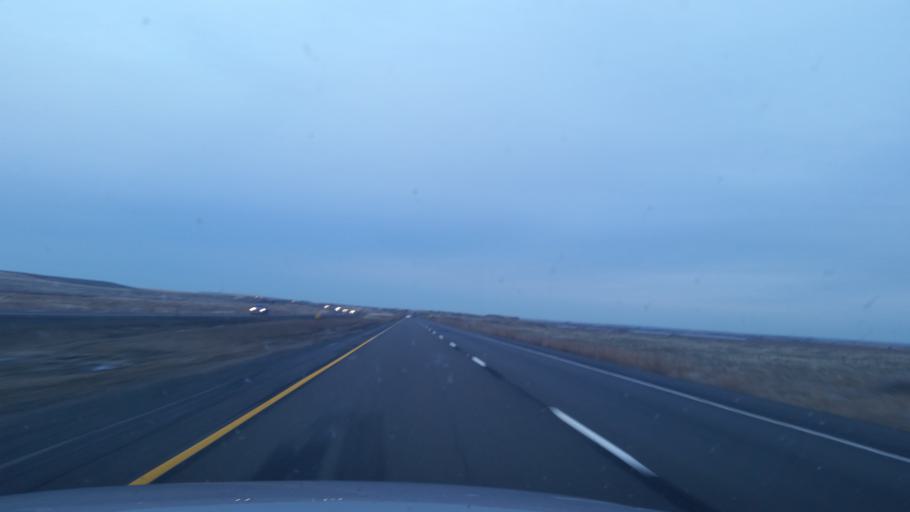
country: US
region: Washington
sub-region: Adams County
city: Ritzville
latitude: 47.2414
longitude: -118.1250
